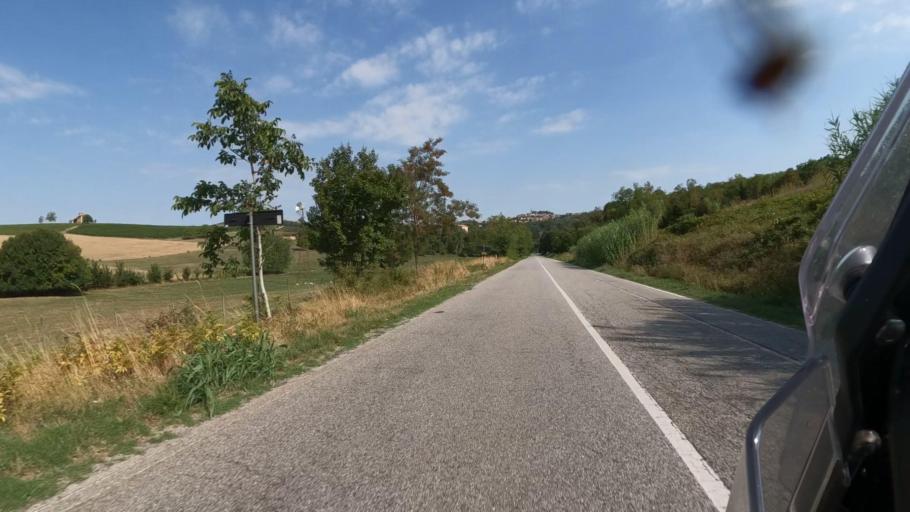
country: IT
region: Piedmont
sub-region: Provincia di Alessandria
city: Vignale Monferrato
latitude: 45.0139
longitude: 8.3886
